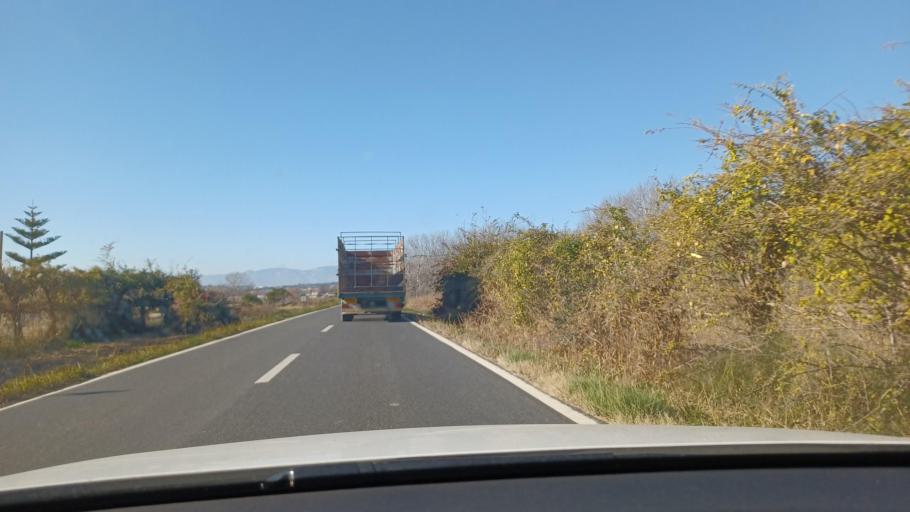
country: ES
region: Catalonia
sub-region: Provincia de Tarragona
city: Amposta
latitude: 40.7045
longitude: 0.6037
